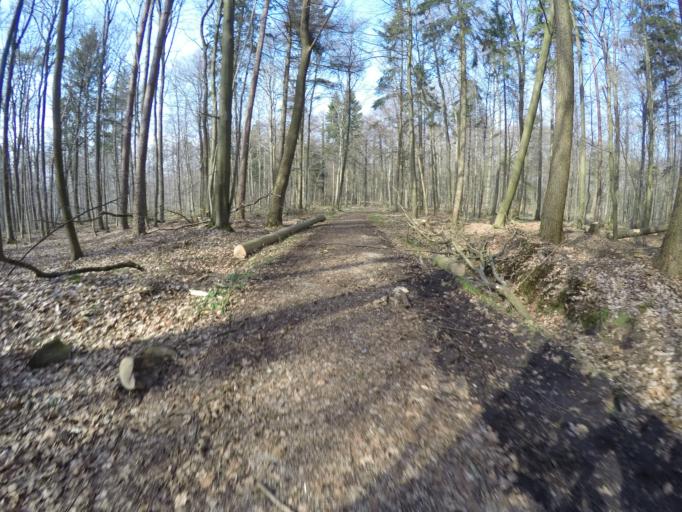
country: DE
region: Schleswig-Holstein
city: Borstel-Hohenraden
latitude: 53.7213
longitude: 9.8255
